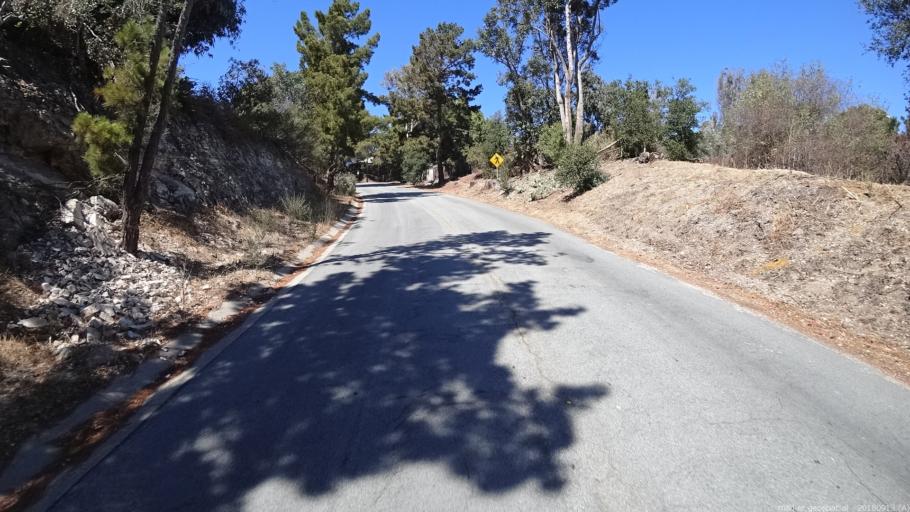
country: US
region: California
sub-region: Monterey County
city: Carmel Valley Village
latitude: 36.5251
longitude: -121.8061
